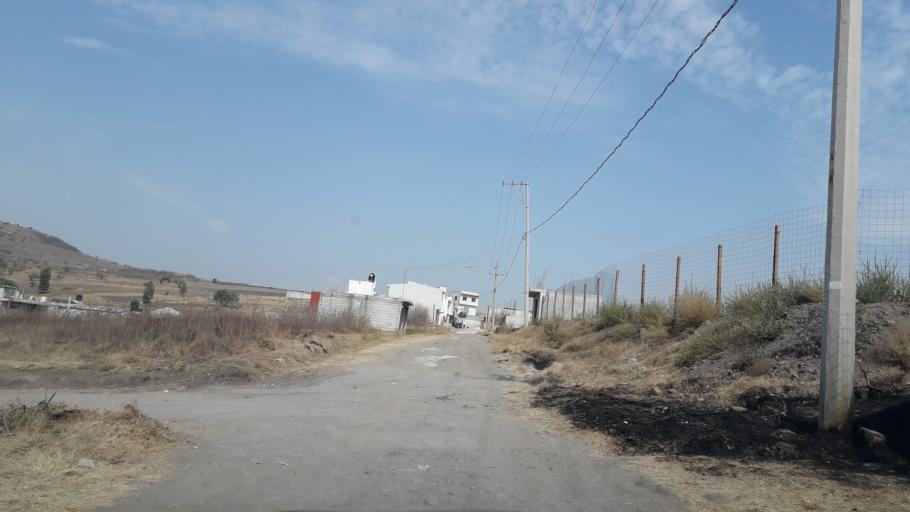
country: MX
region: Puebla
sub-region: Puebla
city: El Capulo (La Quebradora)
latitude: 18.9347
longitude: -98.2684
